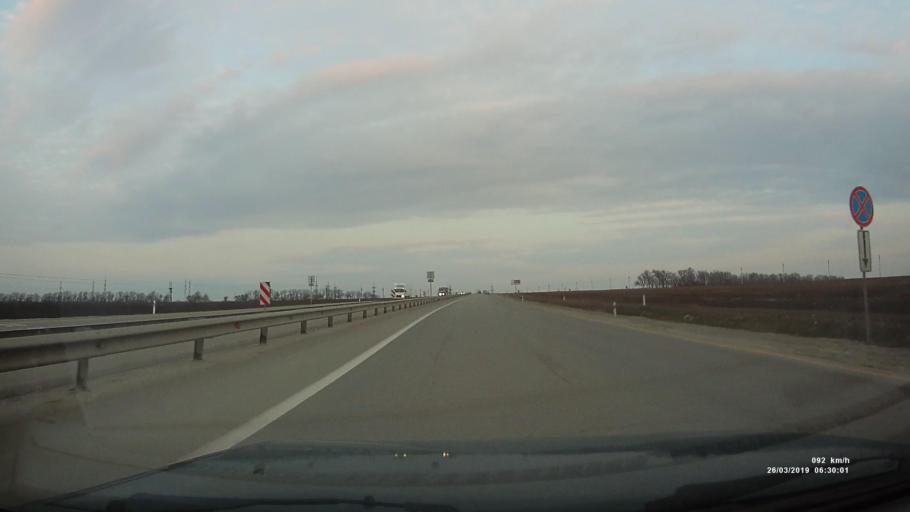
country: RU
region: Rostov
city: Kalinin
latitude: 47.2677
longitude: 39.5621
